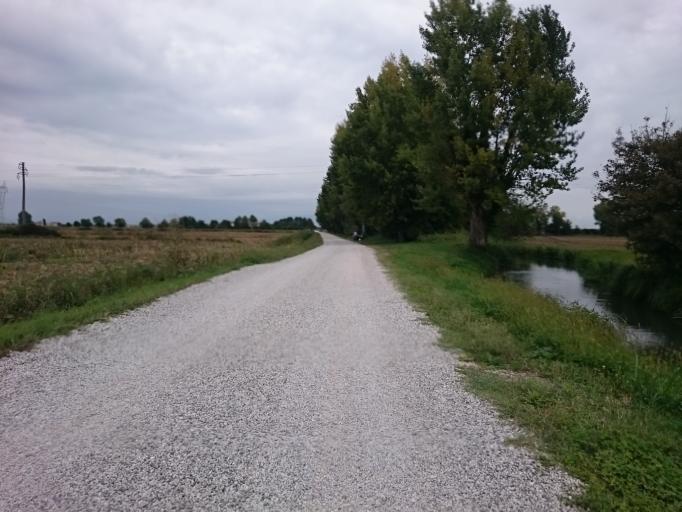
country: IT
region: Veneto
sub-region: Provincia di Vicenza
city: Grumolo delle Abbadesse
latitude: 45.4977
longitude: 11.6598
